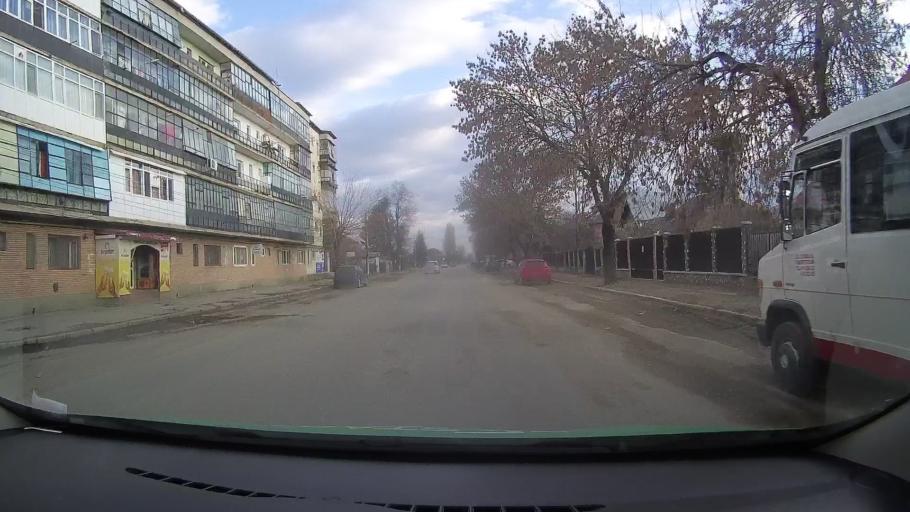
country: RO
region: Dambovita
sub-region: Municipiul Moreni
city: Moreni
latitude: 44.9727
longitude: 25.6497
